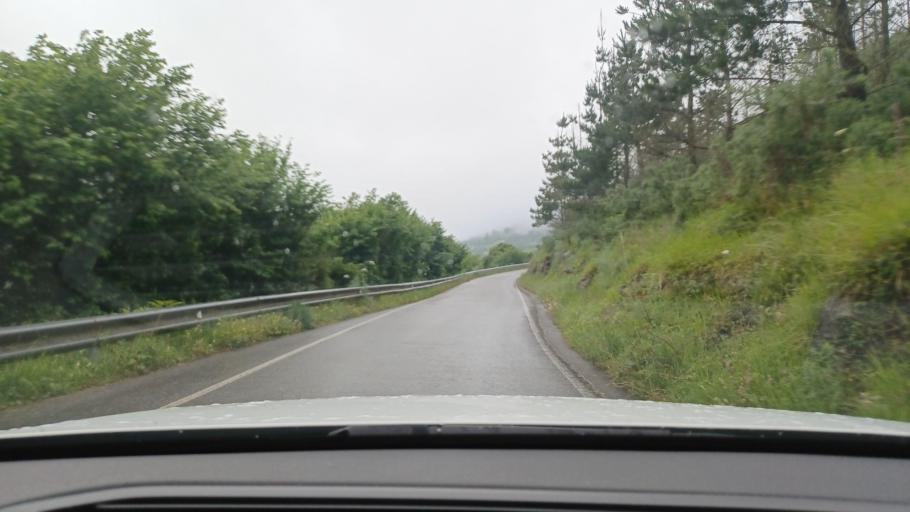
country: ES
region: Asturias
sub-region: Province of Asturias
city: Castandiello
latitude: 43.3002
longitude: -5.9389
